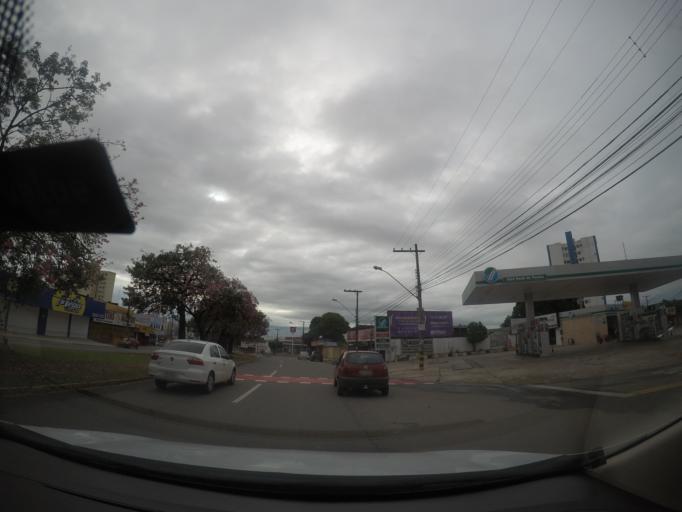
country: BR
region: Goias
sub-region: Goiania
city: Goiania
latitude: -16.7158
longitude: -49.2536
